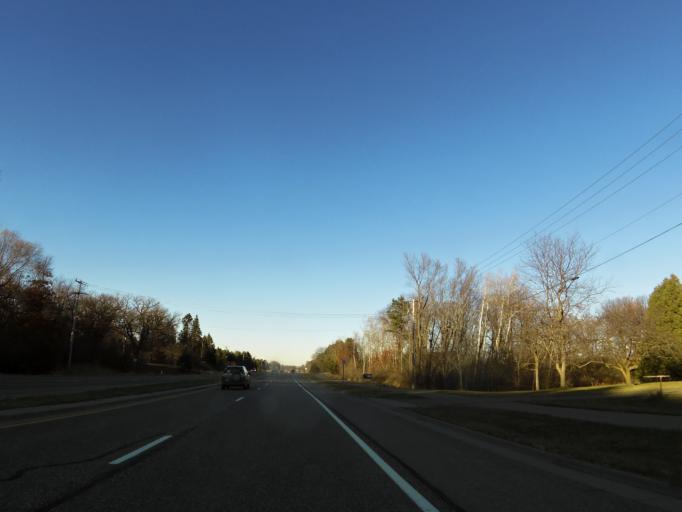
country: US
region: Minnesota
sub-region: Washington County
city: Lake Elmo
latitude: 45.0461
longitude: -92.8629
